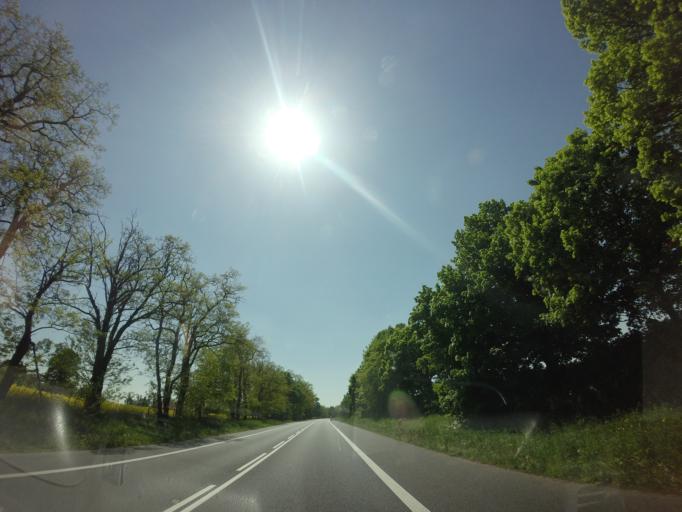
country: PL
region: West Pomeranian Voivodeship
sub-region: Powiat pyrzycki
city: Lipiany
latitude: 52.9800
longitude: 14.9770
